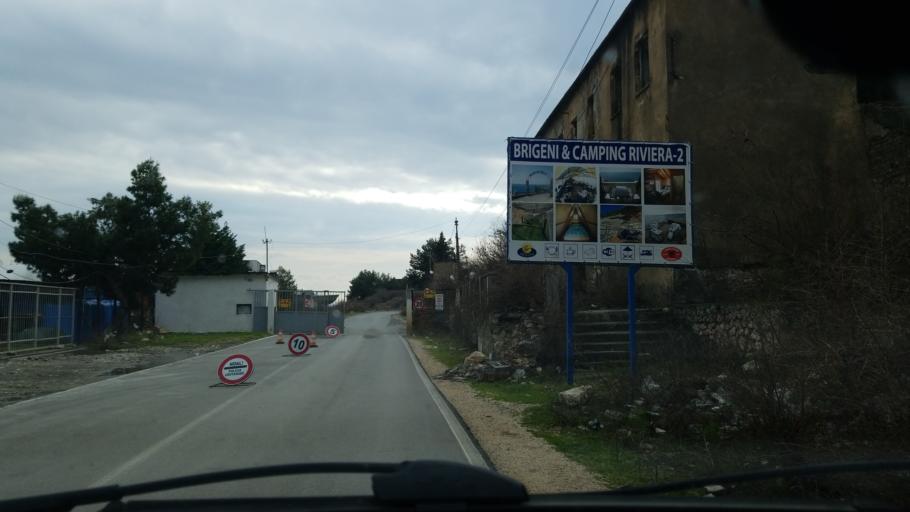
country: AL
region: Lezhe
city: Shengjin
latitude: 41.8139
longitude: 19.5855
